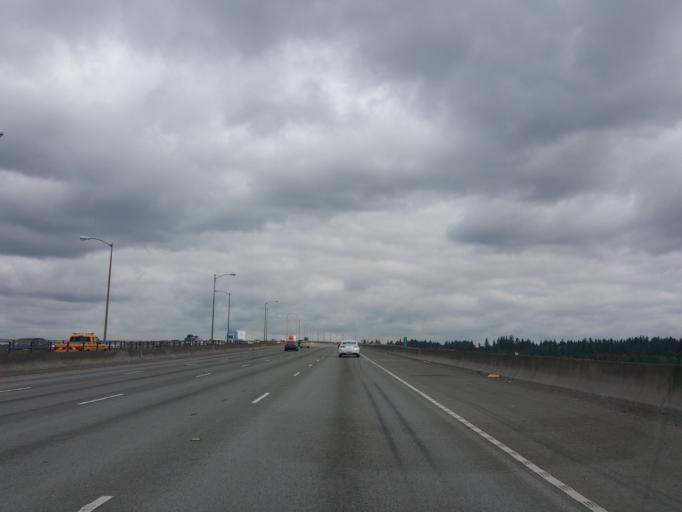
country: US
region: Washington
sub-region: Clark County
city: Mill Plain
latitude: 45.5886
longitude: -122.5456
